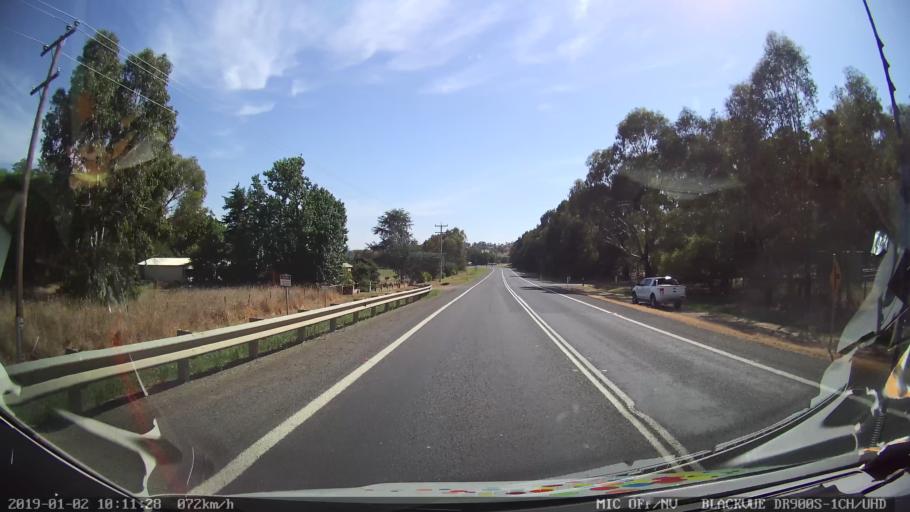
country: AU
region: New South Wales
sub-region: Gundagai
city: Gundagai
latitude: -35.0927
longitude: 148.0922
